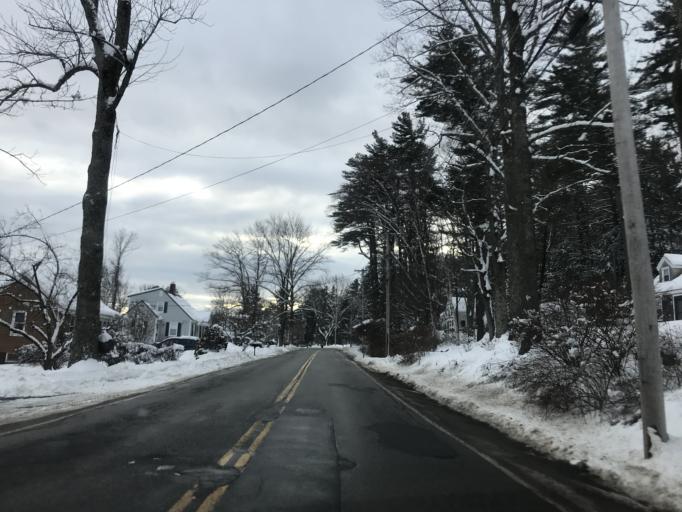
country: US
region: Maine
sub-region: Cumberland County
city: Westbrook
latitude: 43.7236
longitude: -70.3188
